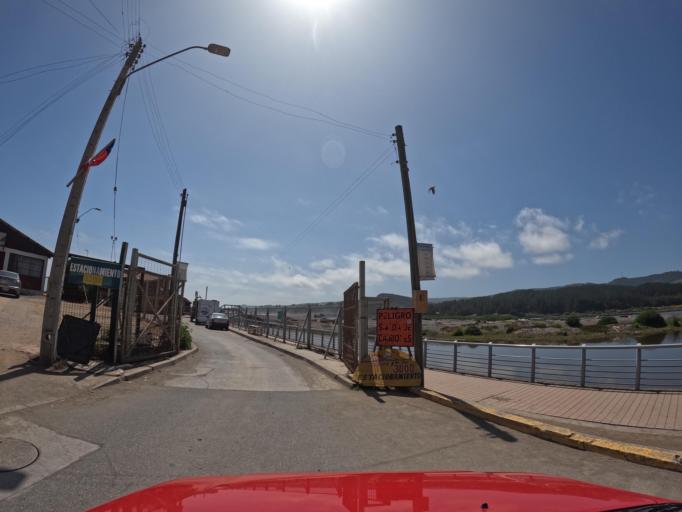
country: CL
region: O'Higgins
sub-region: Provincia de Colchagua
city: Santa Cruz
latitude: -34.6407
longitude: -72.0438
